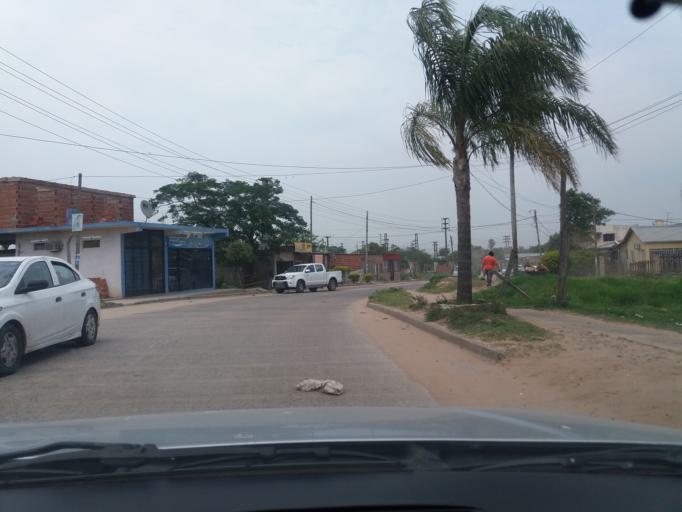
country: AR
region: Corrientes
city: Corrientes
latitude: -27.5094
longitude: -58.7980
